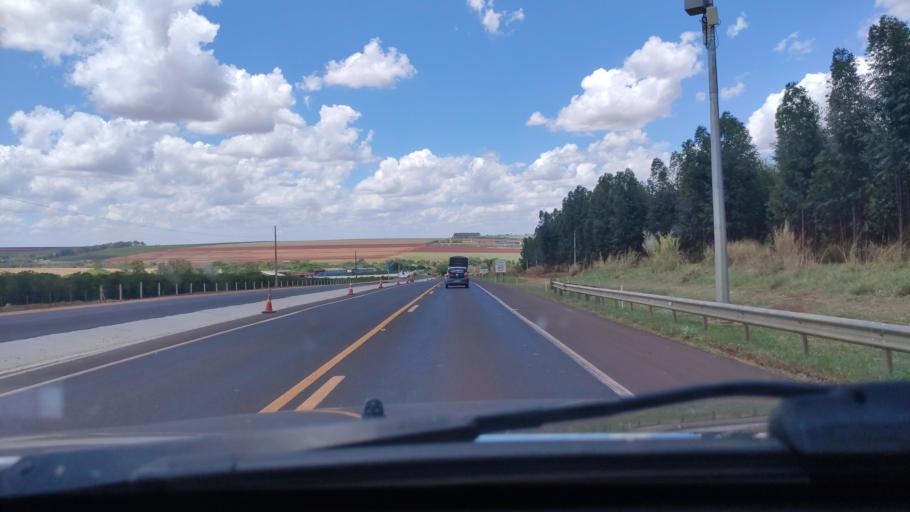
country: BR
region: Sao Paulo
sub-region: Jau
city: Jau
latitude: -22.2247
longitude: -48.5261
